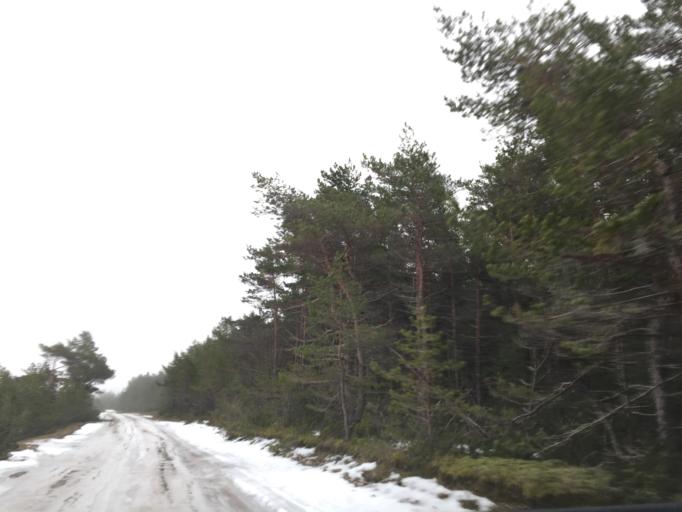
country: EE
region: Saare
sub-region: Kuressaare linn
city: Kuressaare
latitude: 58.5108
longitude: 21.9458
